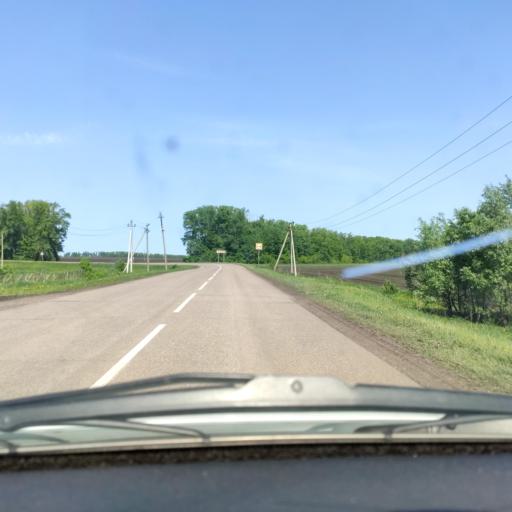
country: RU
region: Bashkortostan
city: Avdon
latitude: 54.5527
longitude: 55.6657
